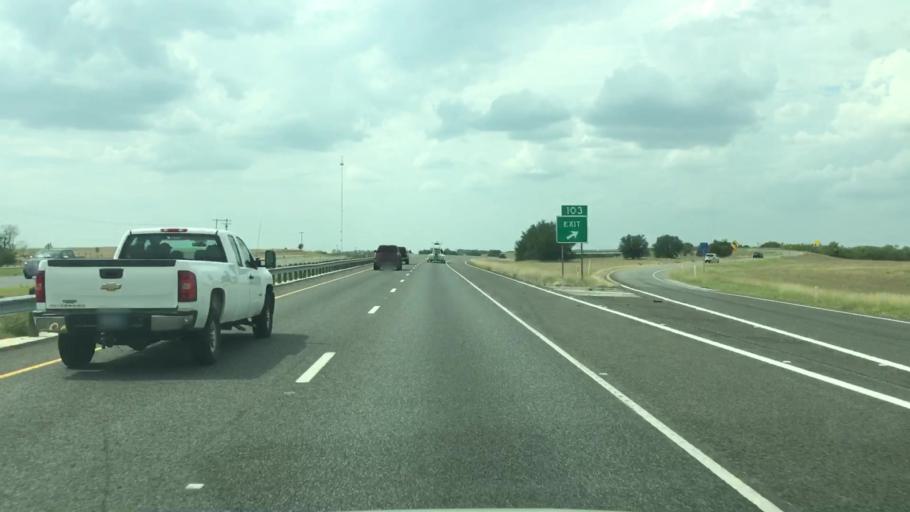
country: US
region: Texas
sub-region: Atascosa County
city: Pleasanton
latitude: 28.9061
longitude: -98.4298
